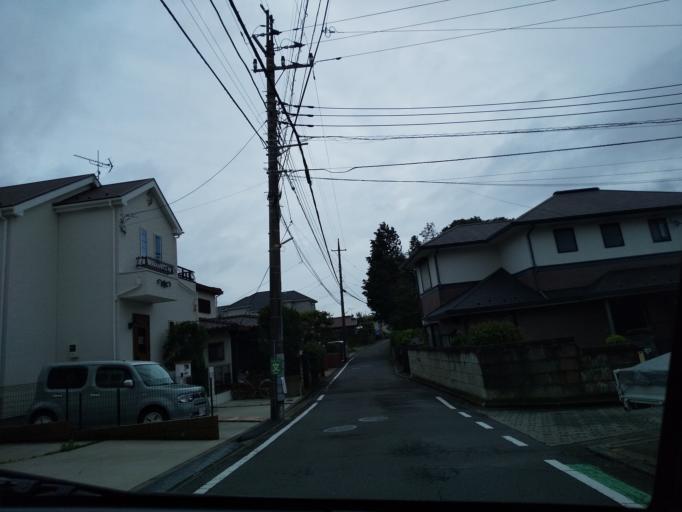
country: JP
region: Kanagawa
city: Fujisawa
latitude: 35.3947
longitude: 139.5138
